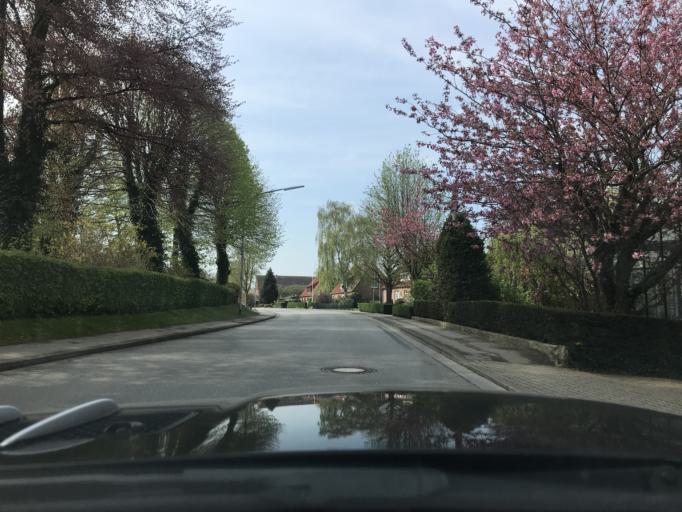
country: DE
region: Schleswig-Holstein
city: Grube
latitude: 54.2273
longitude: 11.0352
